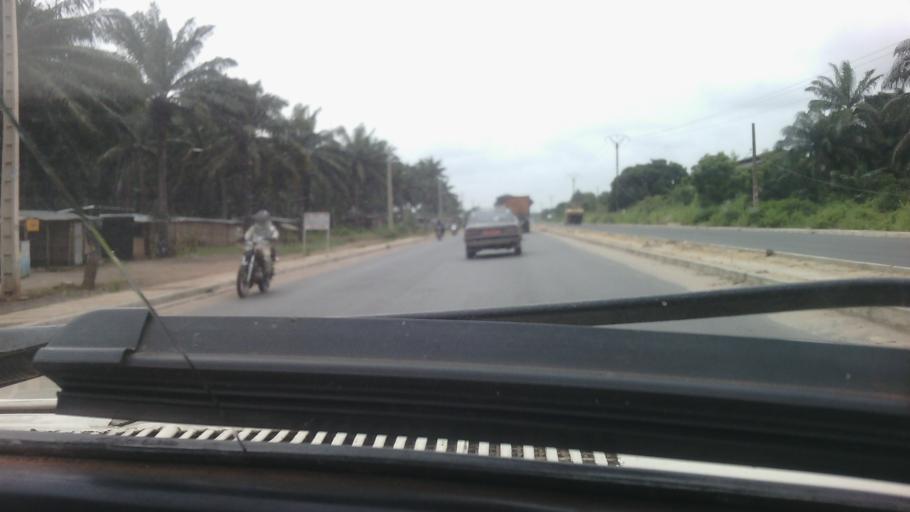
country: BJ
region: Atlantique
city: Hevie
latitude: 6.3820
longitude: 2.1735
